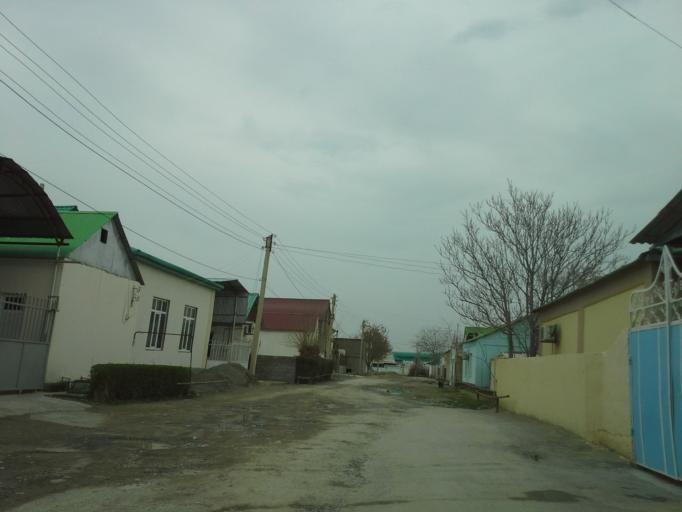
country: TM
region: Ahal
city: Abadan
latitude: 37.9703
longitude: 58.2311
